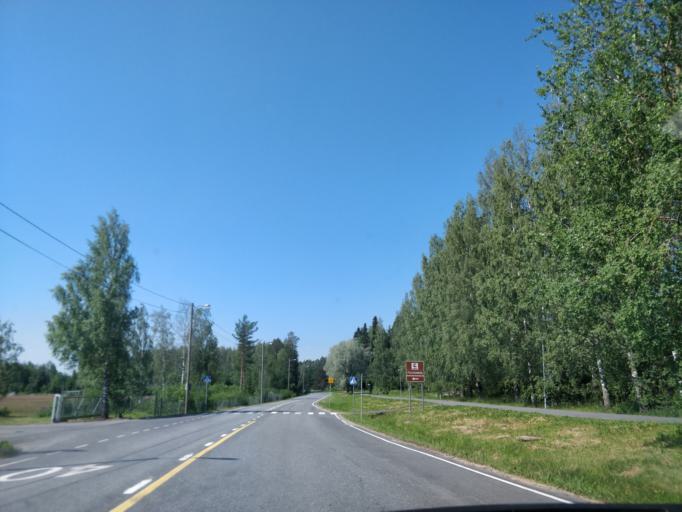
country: FI
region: Haeme
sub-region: Haemeenlinna
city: Tervakoski
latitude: 60.8069
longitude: 24.6072
